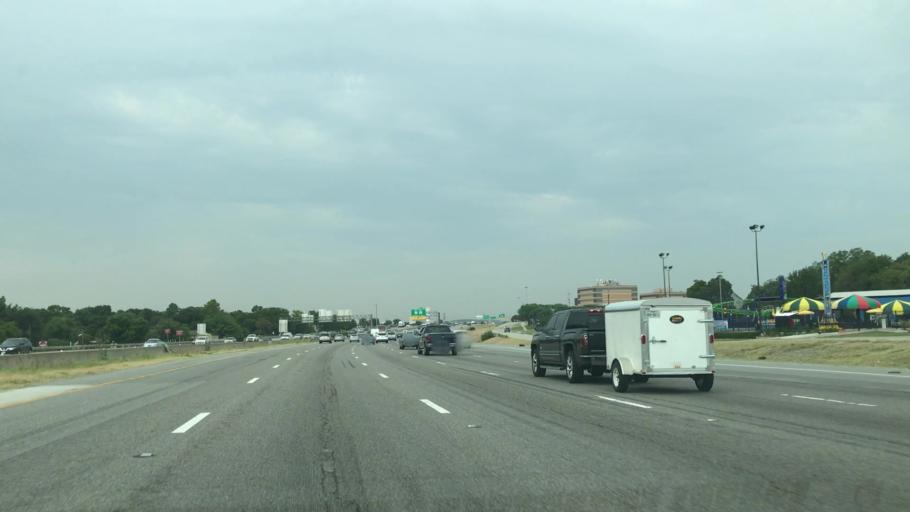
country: US
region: Texas
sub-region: Tarrant County
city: Richland Hills
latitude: 32.8190
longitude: -97.2060
